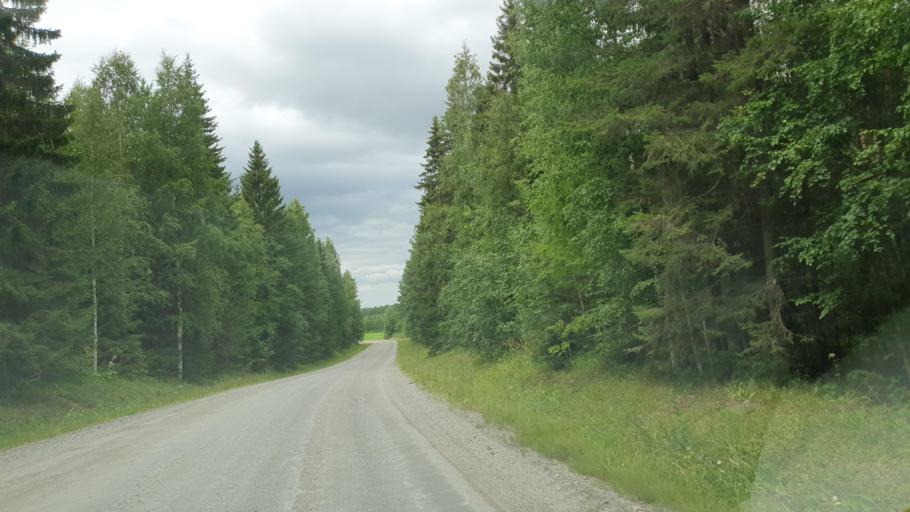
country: FI
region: Northern Savo
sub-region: Ylae-Savo
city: Iisalmi
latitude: 63.5384
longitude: 27.0742
